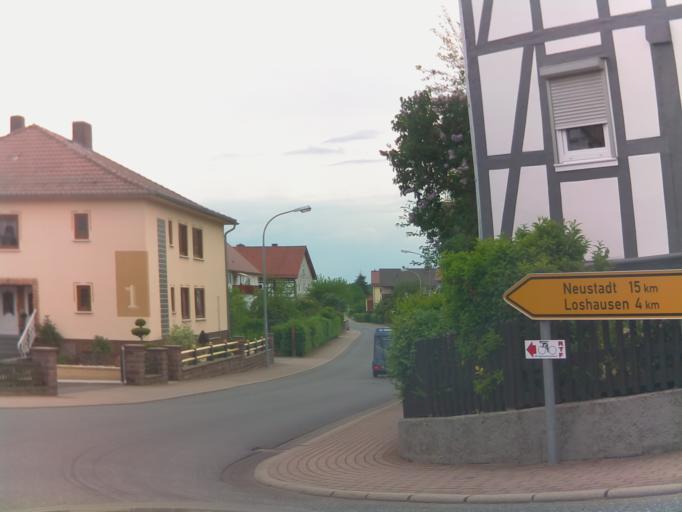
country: DE
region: Hesse
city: Neukirchen
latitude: 50.8782
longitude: 9.3067
